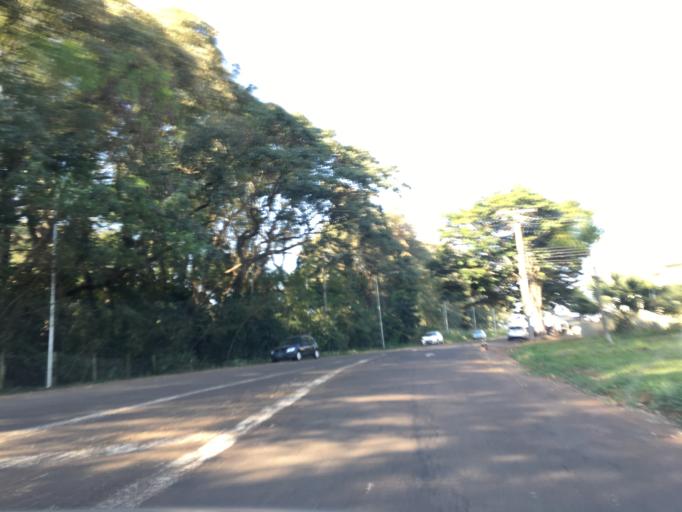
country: BR
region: Sao Paulo
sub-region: Piracicaba
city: Piracicaba
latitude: -22.7151
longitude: -47.6252
